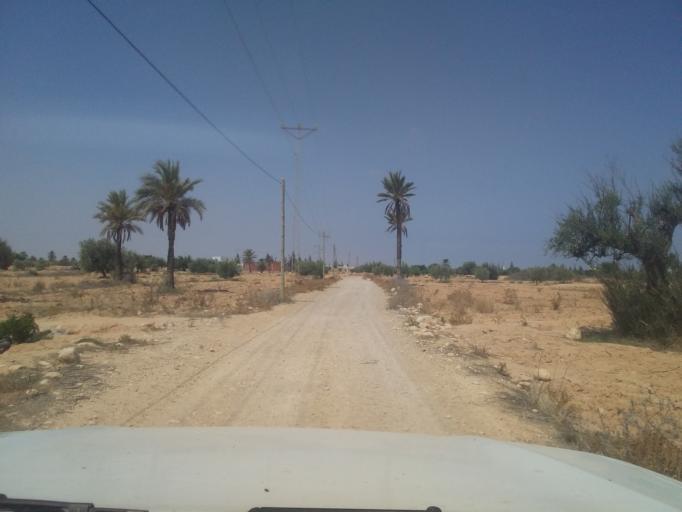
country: TN
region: Qabis
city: Matmata
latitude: 33.5962
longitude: 10.2826
